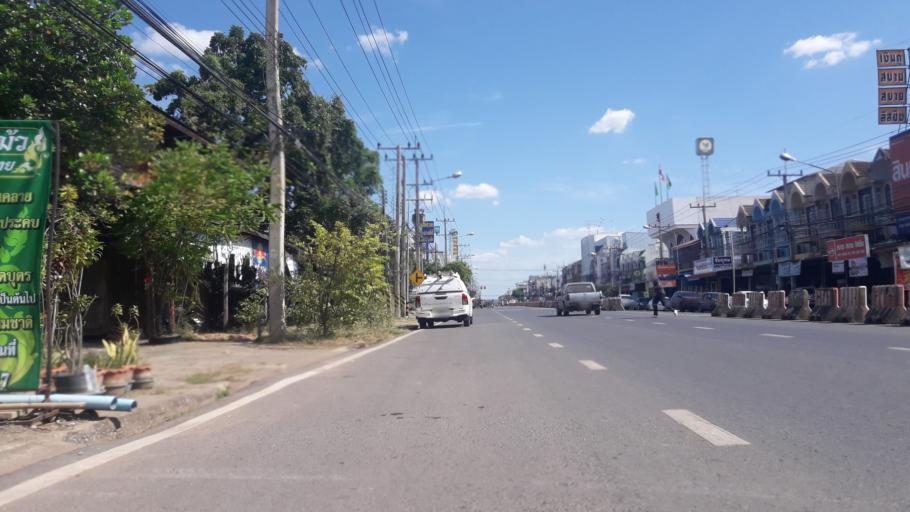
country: TH
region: Phichit
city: Thap Khlo
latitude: 16.1696
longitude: 100.5738
